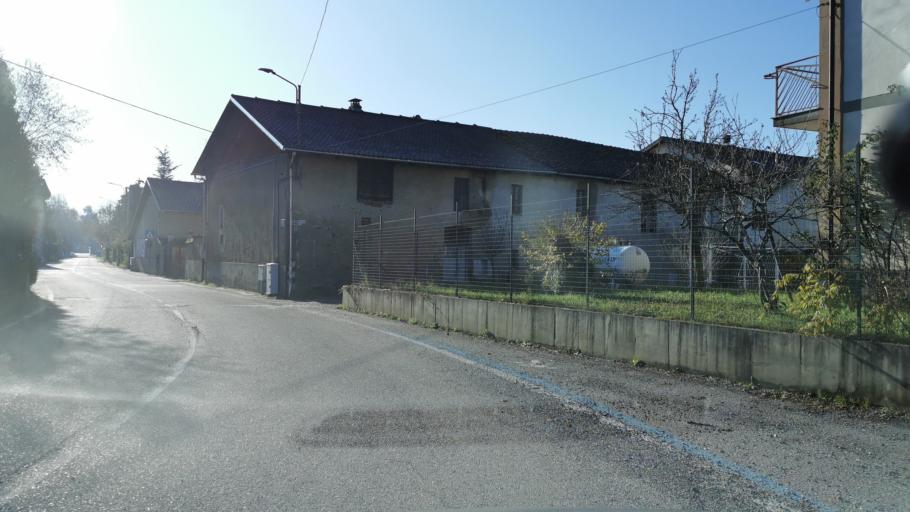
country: IT
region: Piedmont
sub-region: Provincia di Torino
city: Fiano
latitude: 45.2040
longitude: 7.5271
